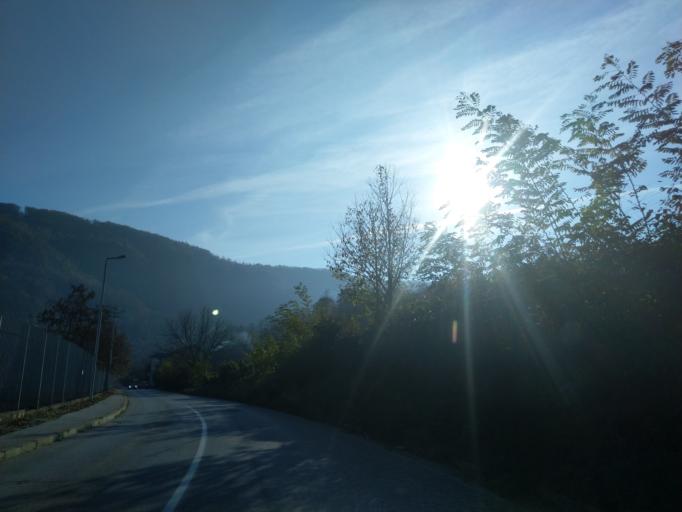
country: RS
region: Central Serbia
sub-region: Zlatiborski Okrug
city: Uzice
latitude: 43.8404
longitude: 19.8856
